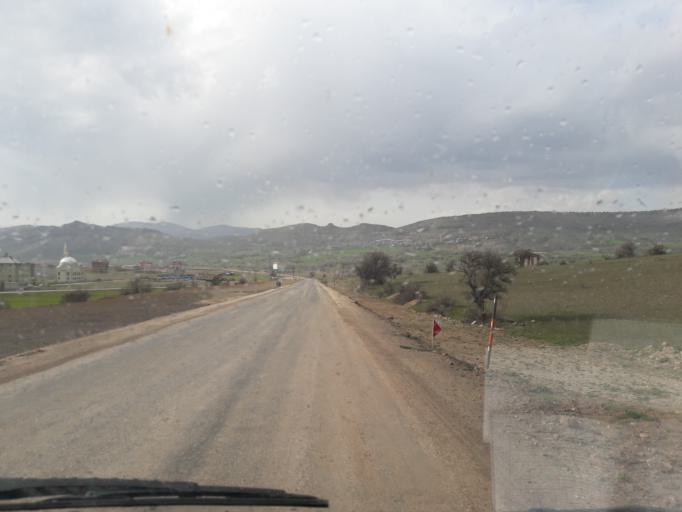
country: TR
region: Giresun
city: Alucra
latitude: 40.3224
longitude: 38.7730
